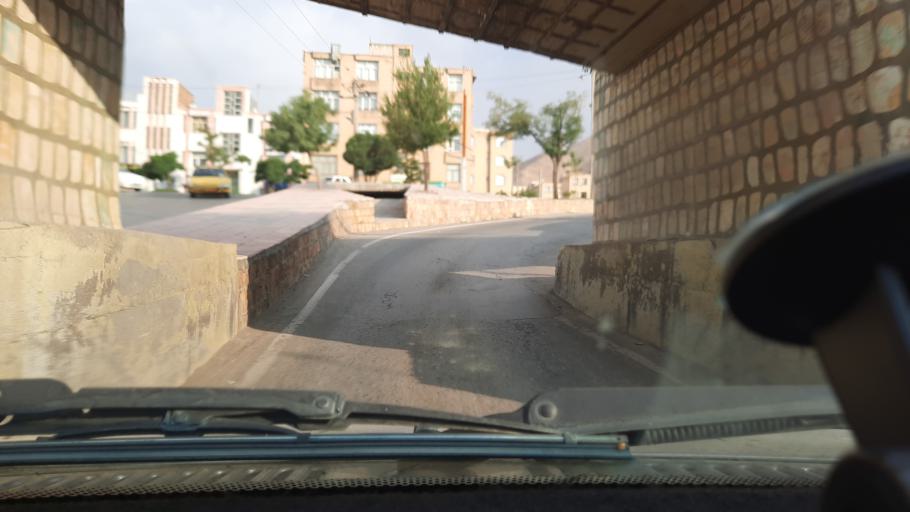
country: IR
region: Markazi
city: Arak
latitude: 34.0713
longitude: 49.6760
